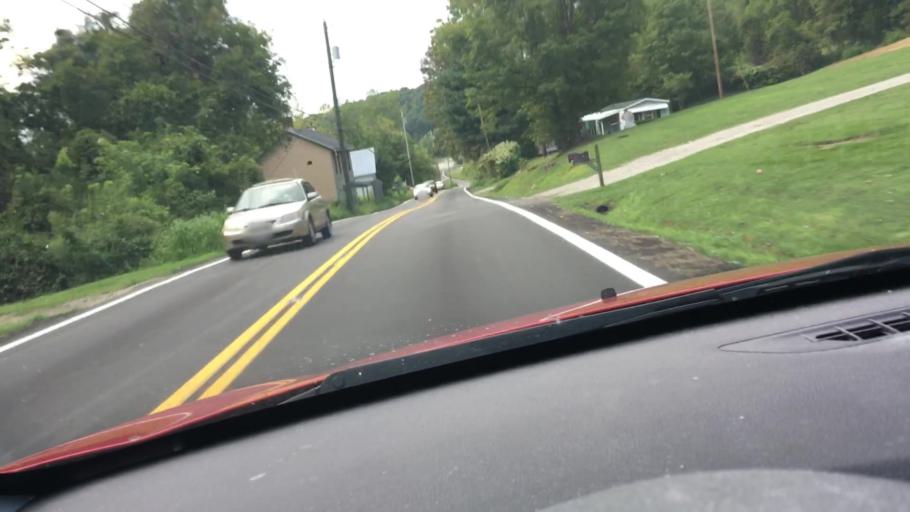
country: US
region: Ohio
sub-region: Athens County
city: Chauncey
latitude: 39.3856
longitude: -82.1379
